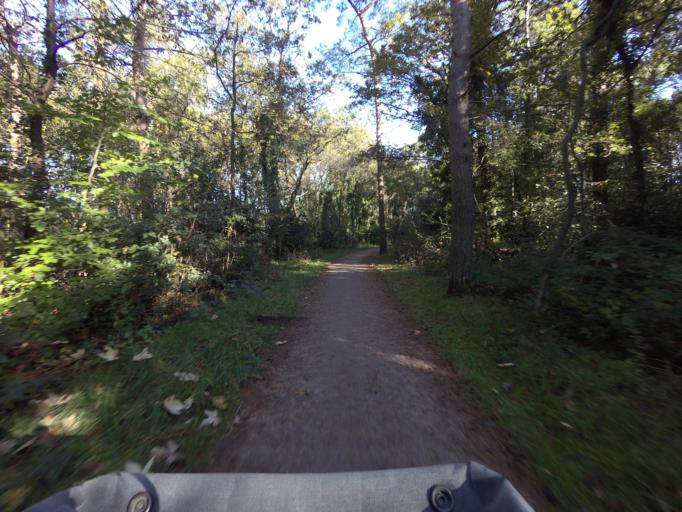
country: NL
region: North Holland
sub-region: Gemeente Laren
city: Laren
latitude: 52.2439
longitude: 5.2360
